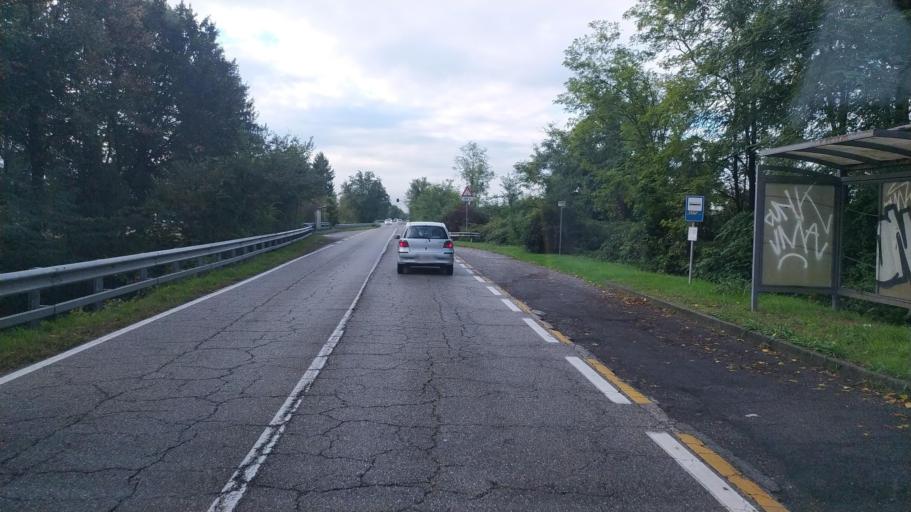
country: IT
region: Lombardy
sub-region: Citta metropolitana di Milano
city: Gaggiano
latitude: 45.3967
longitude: 9.0302
